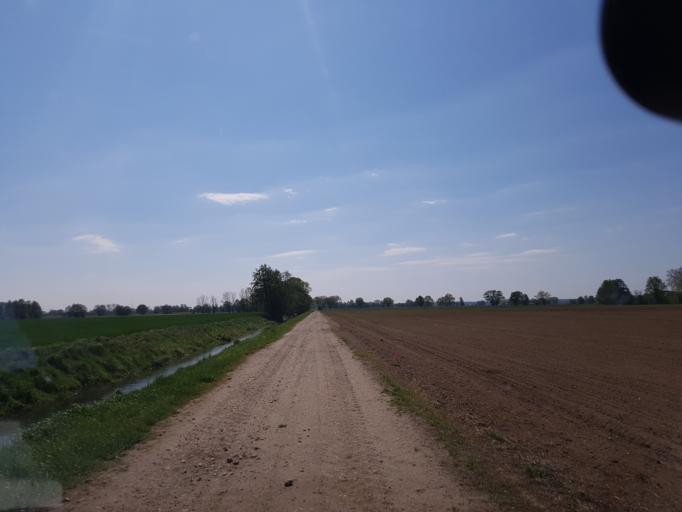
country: DE
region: Brandenburg
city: Schonewalde
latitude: 51.6801
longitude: 13.5850
